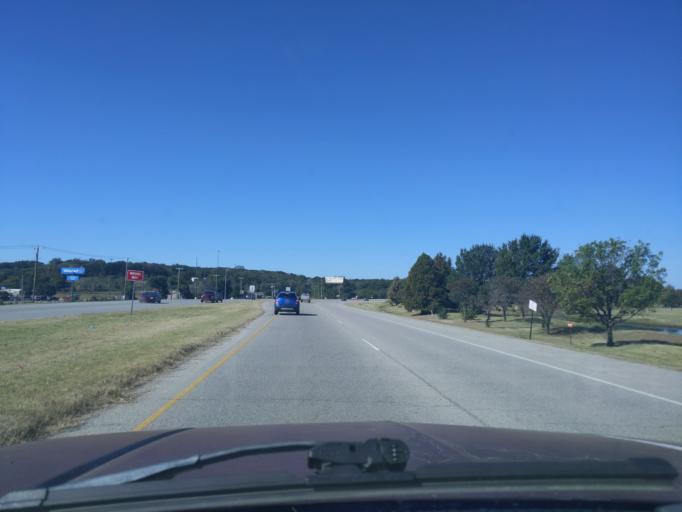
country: US
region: Oklahoma
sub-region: Creek County
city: Sapulpa
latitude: 35.9884
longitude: -96.1327
